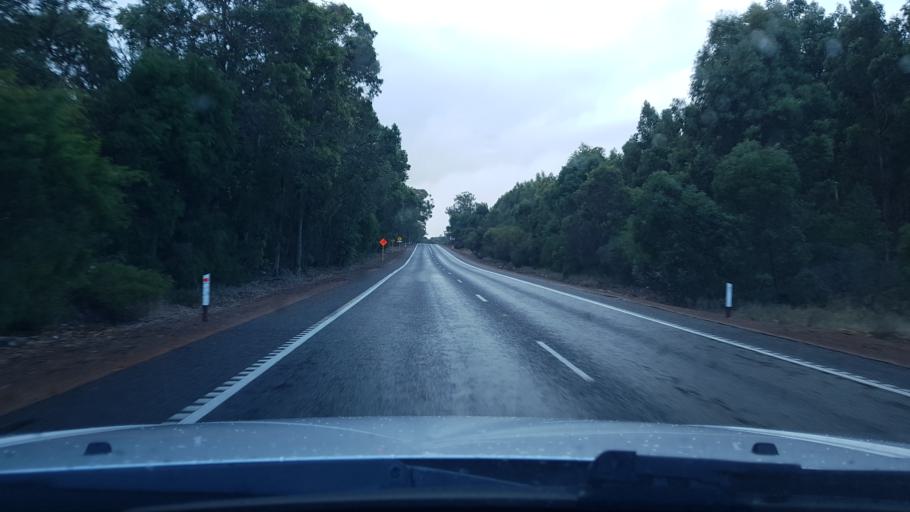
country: AU
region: Western Australia
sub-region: Augusta-Margaret River Shire
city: Margaret River
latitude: -33.8864
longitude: 115.0874
